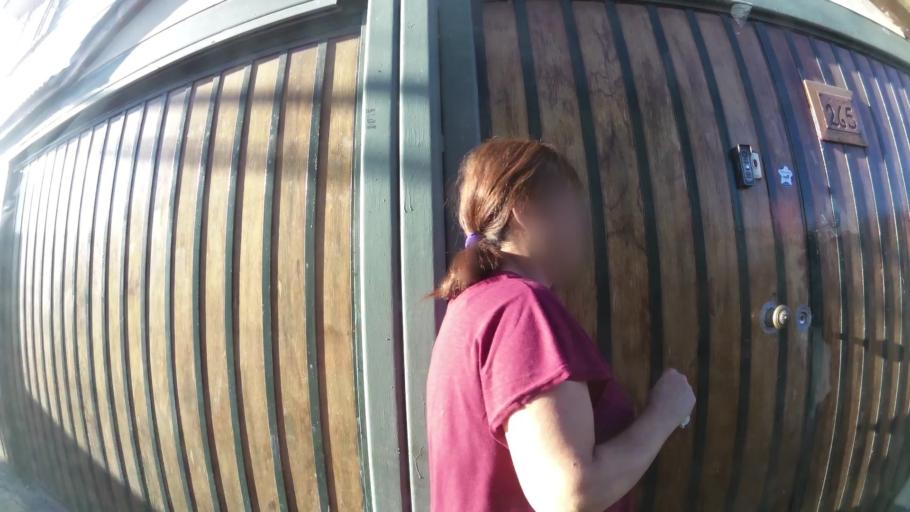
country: CL
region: Valparaiso
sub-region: Provincia de Valparaiso
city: Valparaiso
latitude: -33.0564
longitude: -71.6125
